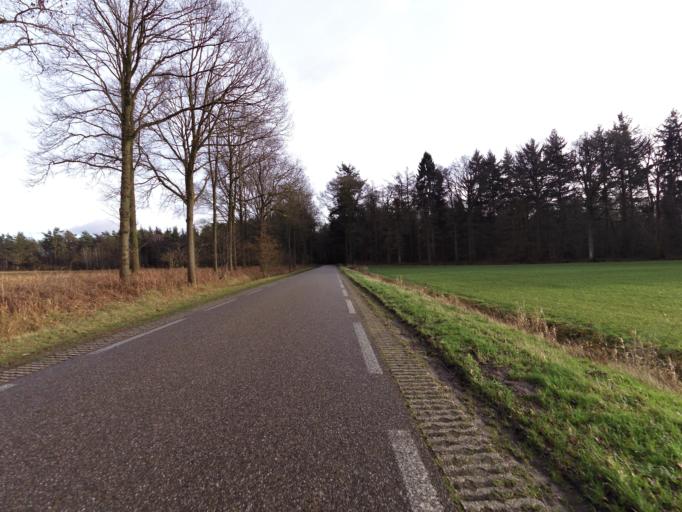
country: NL
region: Gelderland
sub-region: Gemeente Bronckhorst
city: Zelhem
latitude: 51.9691
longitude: 6.3663
